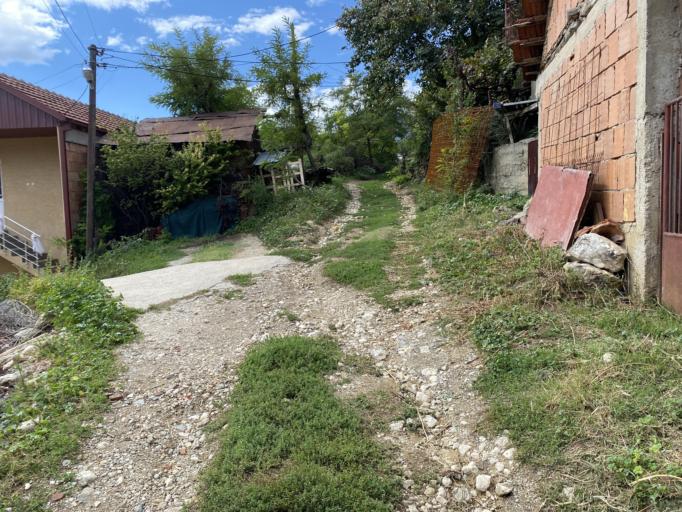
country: MK
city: Radishani
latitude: 42.1087
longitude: 21.4529
